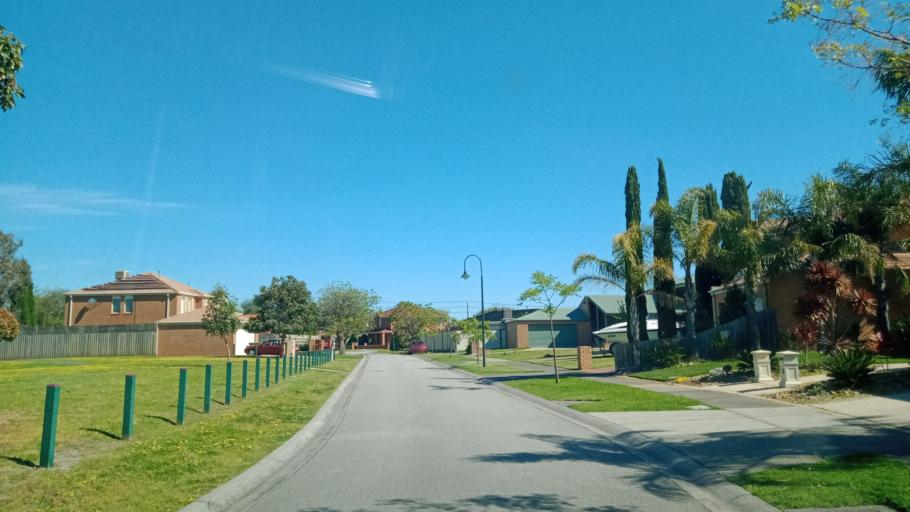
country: AU
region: Victoria
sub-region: Monash
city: Oakleigh South
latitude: -37.9360
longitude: 145.0728
